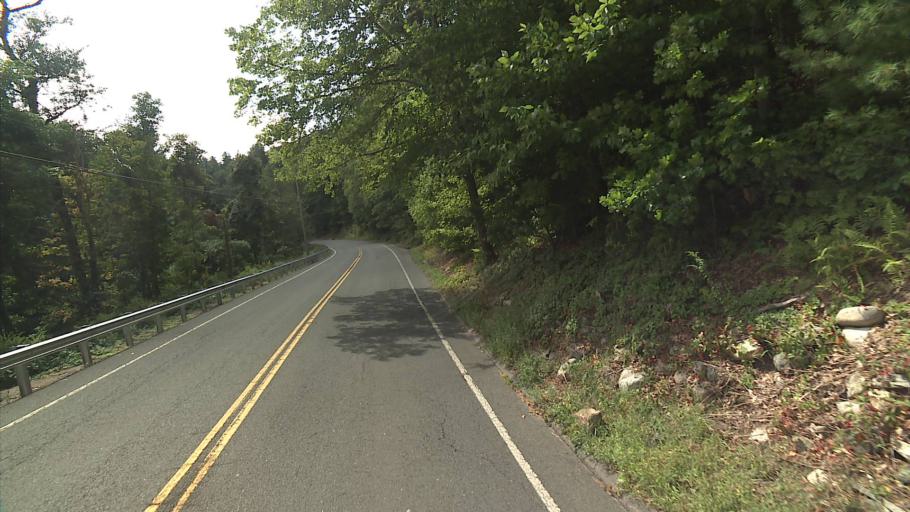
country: US
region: Massachusetts
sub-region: Hampden County
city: Granville
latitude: 42.0309
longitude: -72.8629
